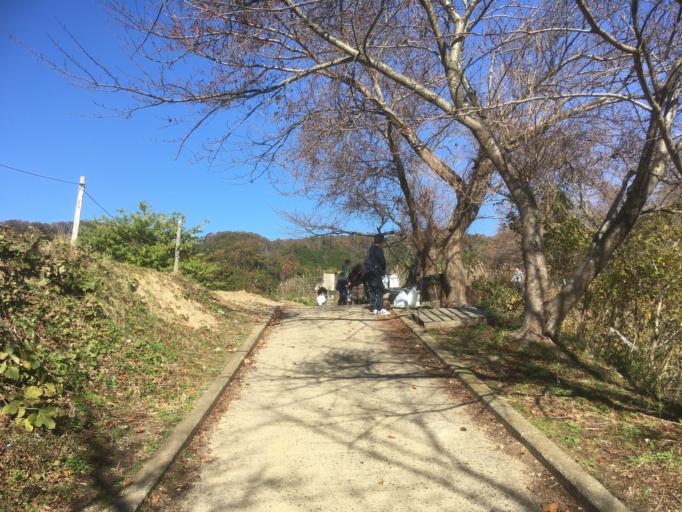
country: JP
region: Osaka
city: Kashihara
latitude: 34.6048
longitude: 135.6595
